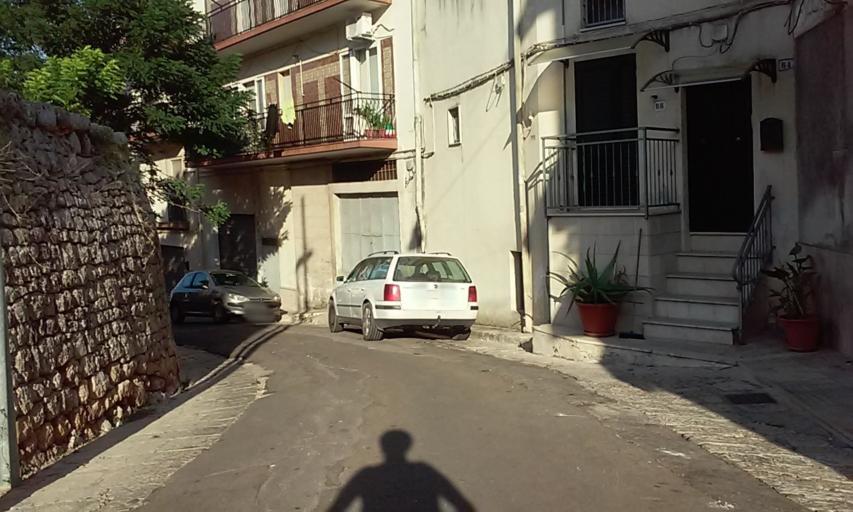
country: IT
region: Apulia
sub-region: Provincia di Brindisi
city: Ceglie Messapica
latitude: 40.6457
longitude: 17.5204
